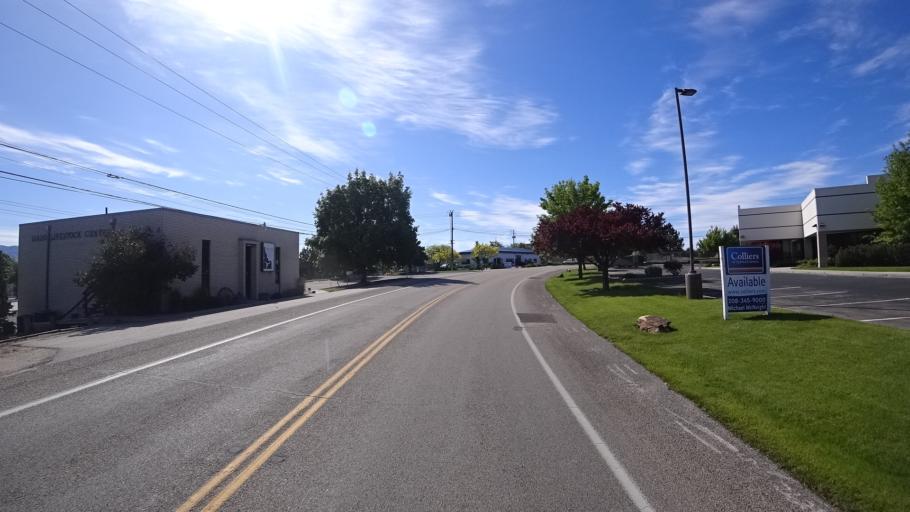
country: US
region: Idaho
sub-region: Ada County
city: Boise
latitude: 43.5688
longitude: -116.2079
